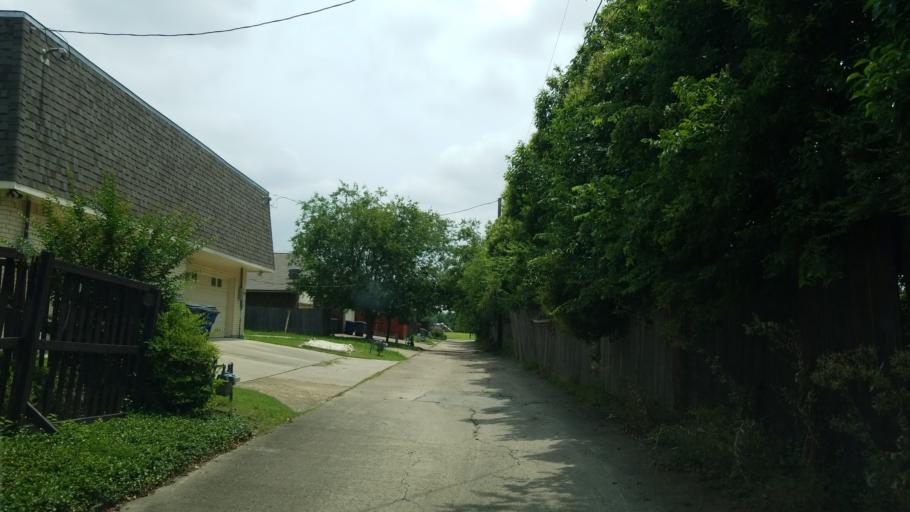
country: US
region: Texas
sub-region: Dallas County
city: Farmers Branch
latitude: 32.9078
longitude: -96.8780
